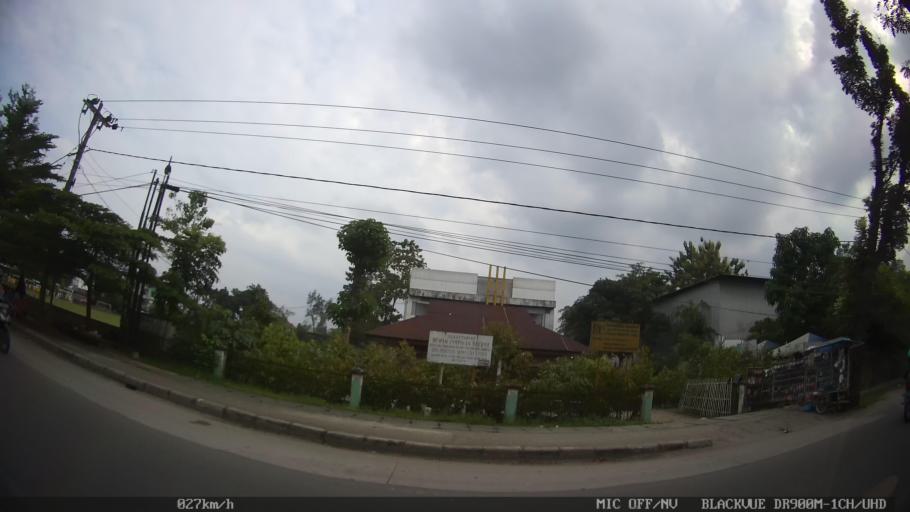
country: ID
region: North Sumatra
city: Deli Tua
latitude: 3.5414
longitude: 98.6783
